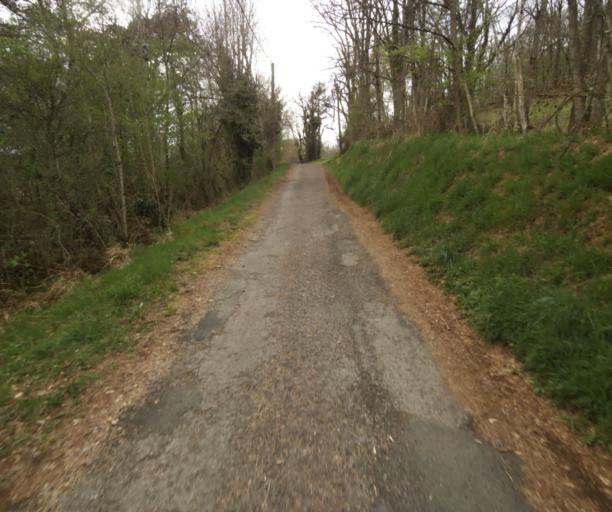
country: FR
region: Limousin
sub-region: Departement de la Correze
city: Tulle
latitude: 45.2578
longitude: 1.7783
